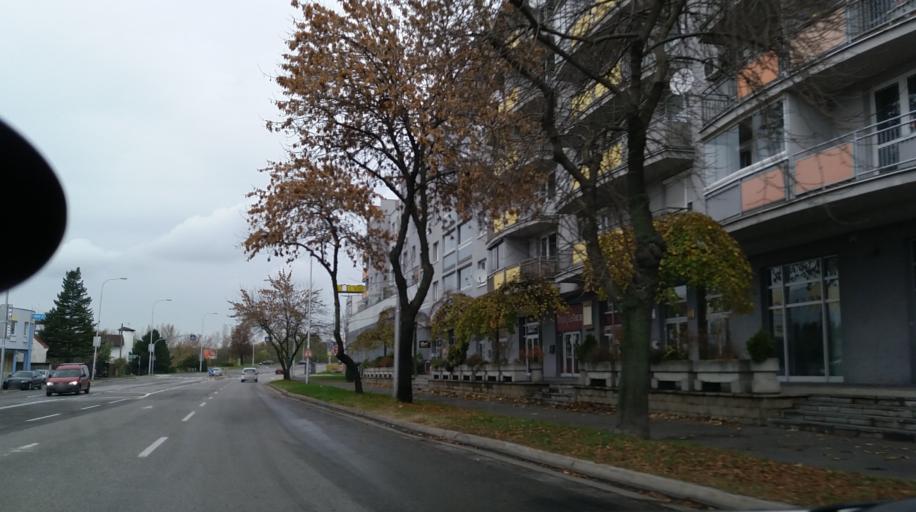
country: SK
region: Bratislavsky
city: Bratislava
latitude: 48.1275
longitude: 17.0948
